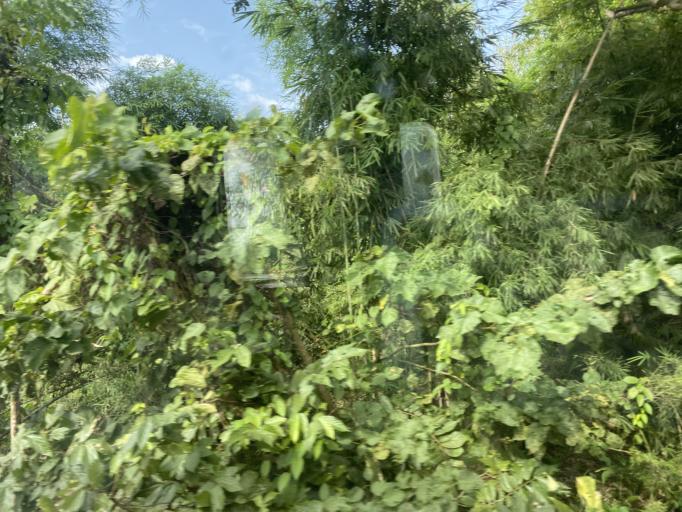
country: IN
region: Tripura
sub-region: West Tripura
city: Agartala
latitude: 23.9889
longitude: 91.2841
